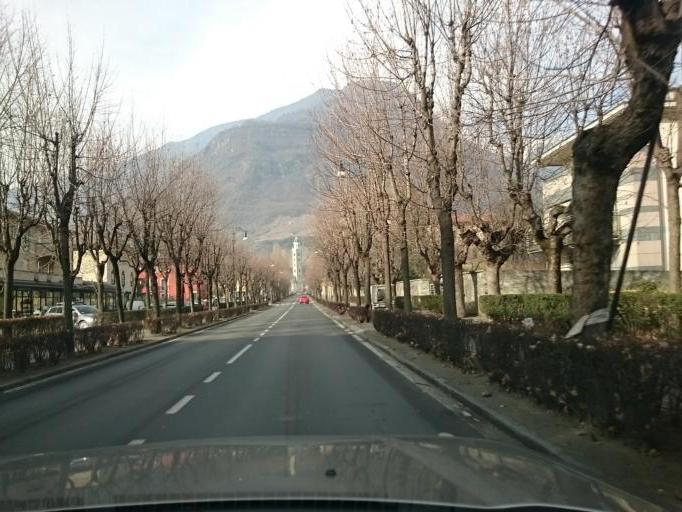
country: IT
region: Lombardy
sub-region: Provincia di Sondrio
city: Tirano
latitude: 46.2173
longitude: 10.1615
